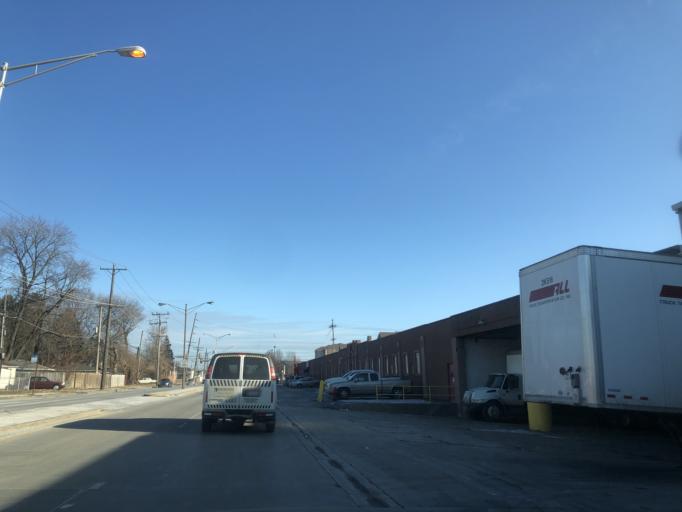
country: US
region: Illinois
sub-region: Cook County
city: Hometown
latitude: 41.7746
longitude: -87.7494
